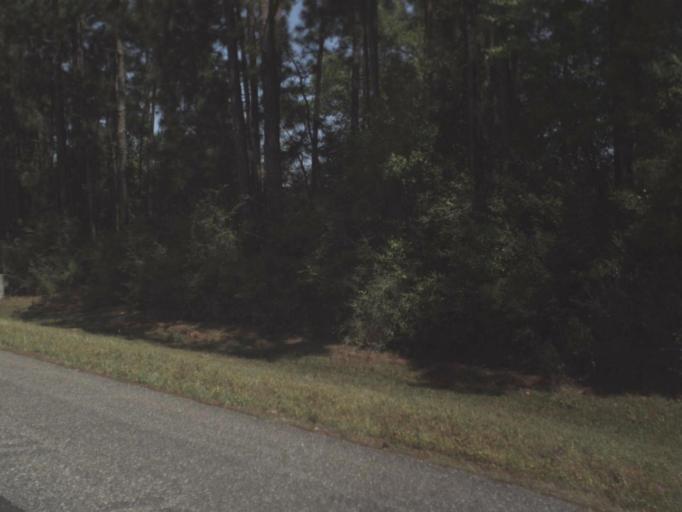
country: US
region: Florida
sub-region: Escambia County
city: Cantonment
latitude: 30.5438
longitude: -87.3478
